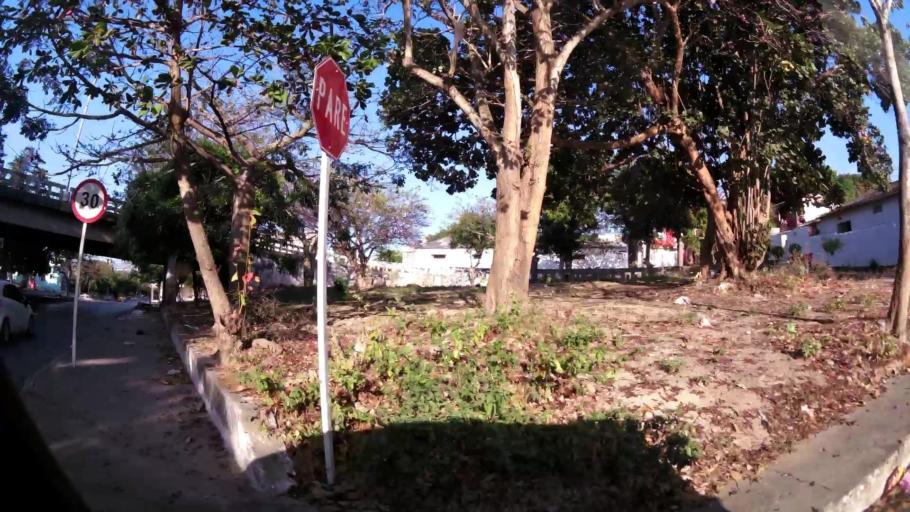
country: CO
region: Atlantico
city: Barranquilla
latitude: 10.9830
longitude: -74.8021
